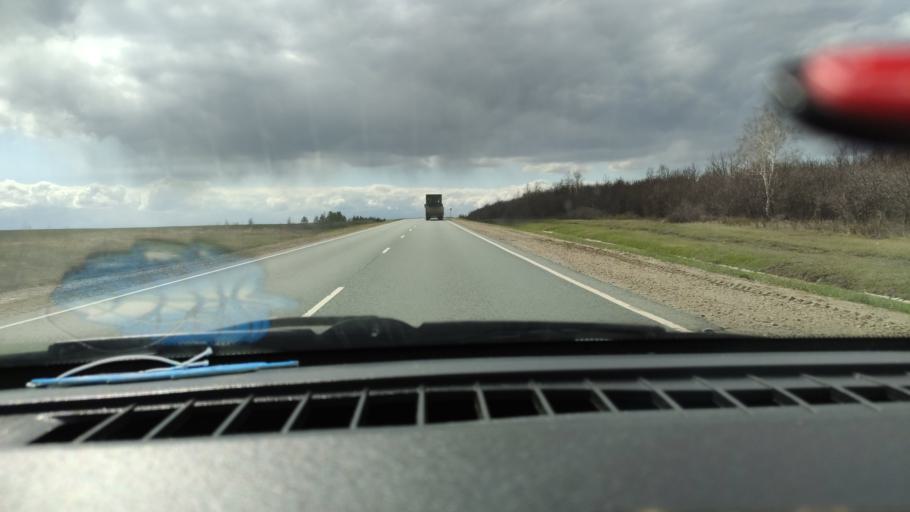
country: RU
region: Saratov
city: Alekseyevka
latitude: 52.2363
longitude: 47.9047
